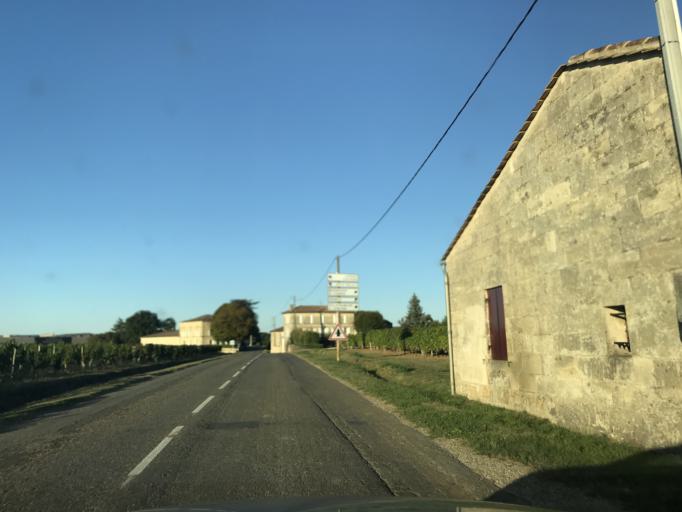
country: FR
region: Aquitaine
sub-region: Departement de la Gironde
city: Lussac
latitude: 44.9330
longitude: -0.0730
